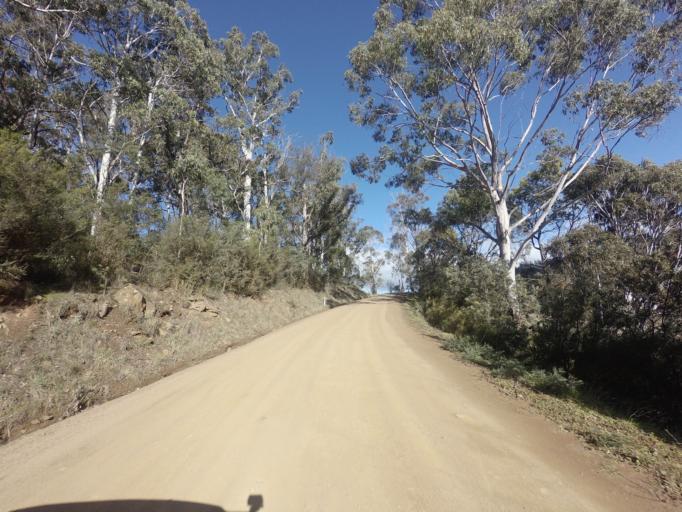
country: AU
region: Tasmania
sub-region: Derwent Valley
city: New Norfolk
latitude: -42.7081
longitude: 147.0221
